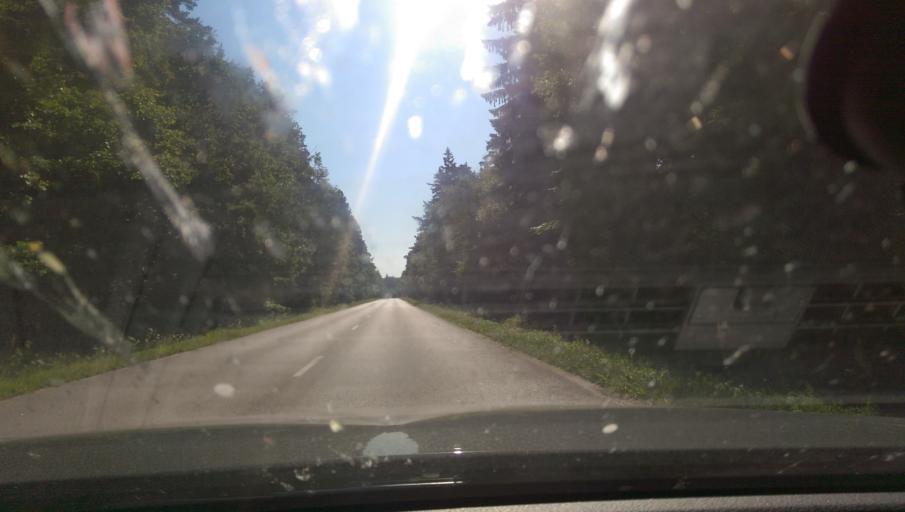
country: LT
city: Priekule
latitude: 55.6370
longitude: 21.3226
